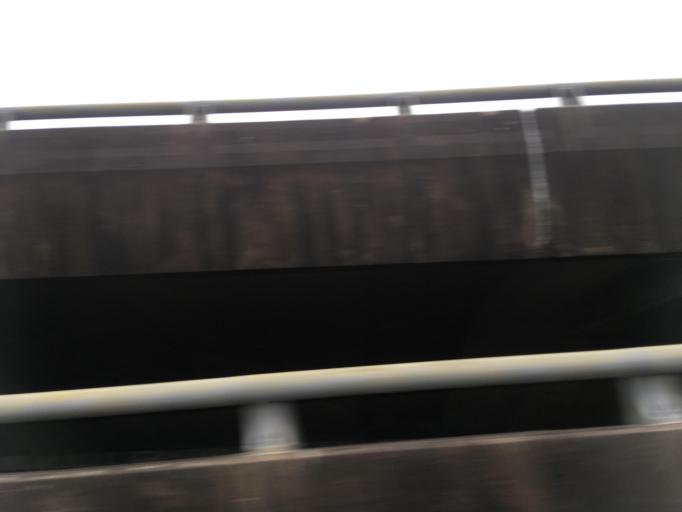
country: TW
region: Taiwan
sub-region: Yilan
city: Yilan
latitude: 24.6988
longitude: 121.7911
